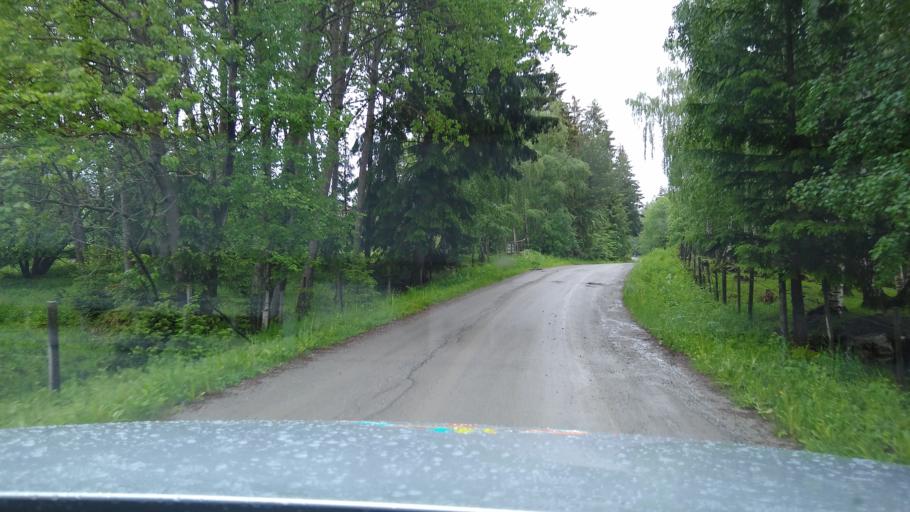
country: NO
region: Oppland
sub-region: Ringebu
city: Ringebu
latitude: 61.5429
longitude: 10.1070
